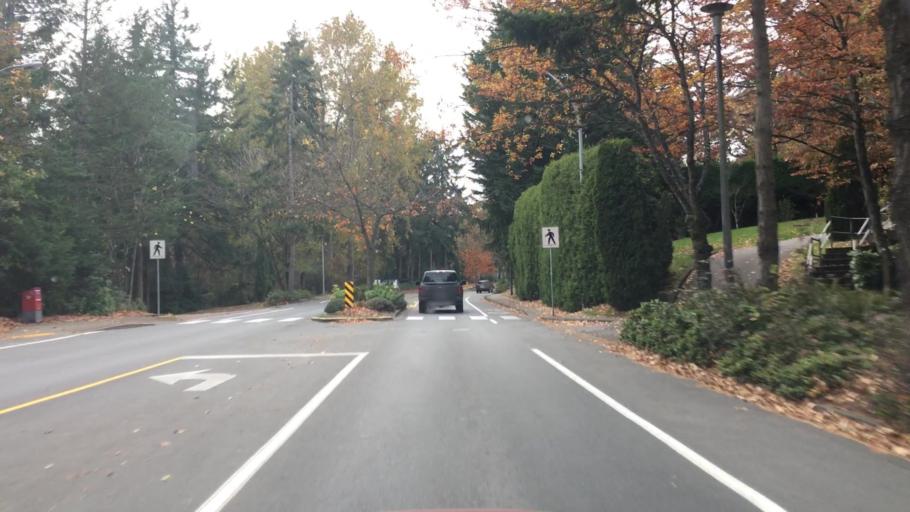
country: CA
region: British Columbia
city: Victoria
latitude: 48.4985
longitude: -123.3698
